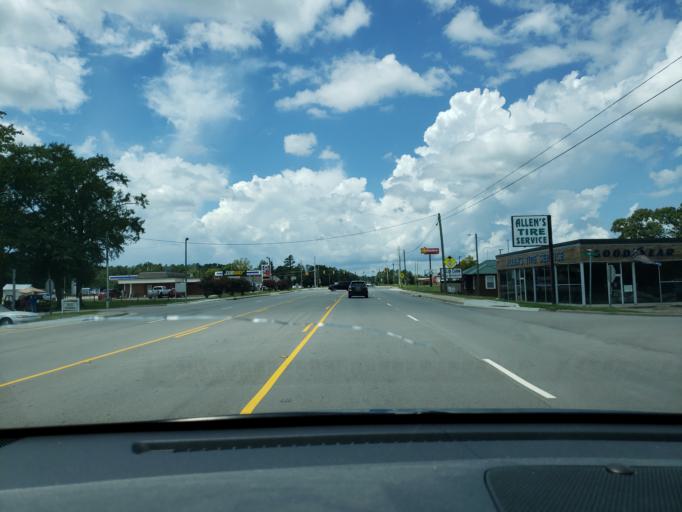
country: US
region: North Carolina
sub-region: Bladen County
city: Bladenboro
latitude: 34.7331
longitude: -78.7904
